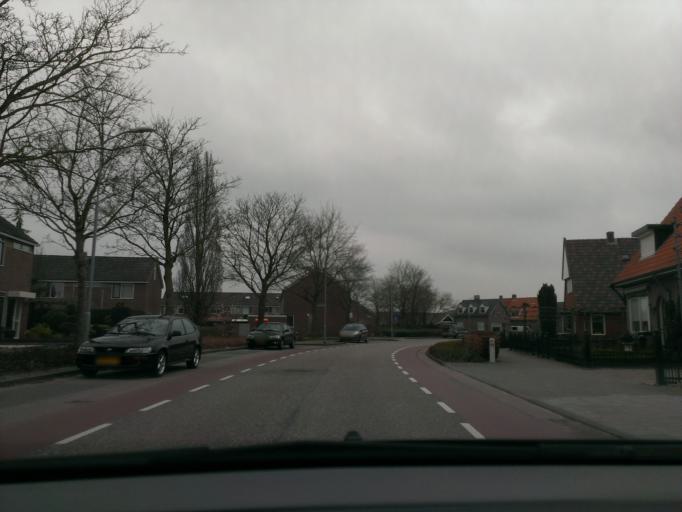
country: NL
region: Gelderland
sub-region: Gemeente Hattem
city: Hattem
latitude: 52.4756
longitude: 6.0533
